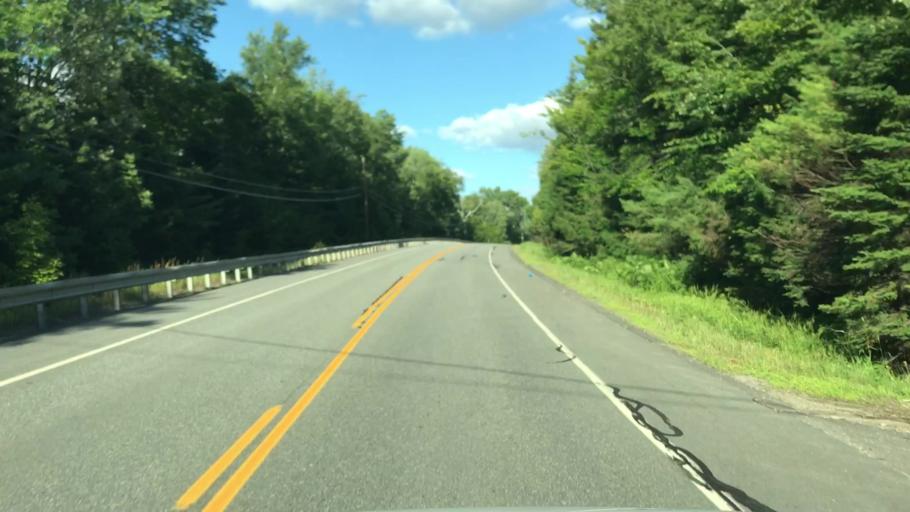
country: US
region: Maine
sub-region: Penobscot County
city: Lincoln
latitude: 45.3789
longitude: -68.4514
